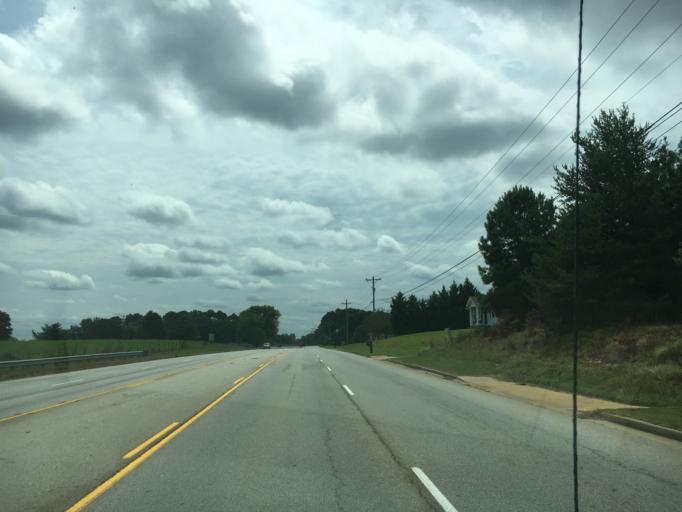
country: US
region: South Carolina
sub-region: Spartanburg County
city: Roebuck
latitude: 34.8413
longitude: -82.0010
